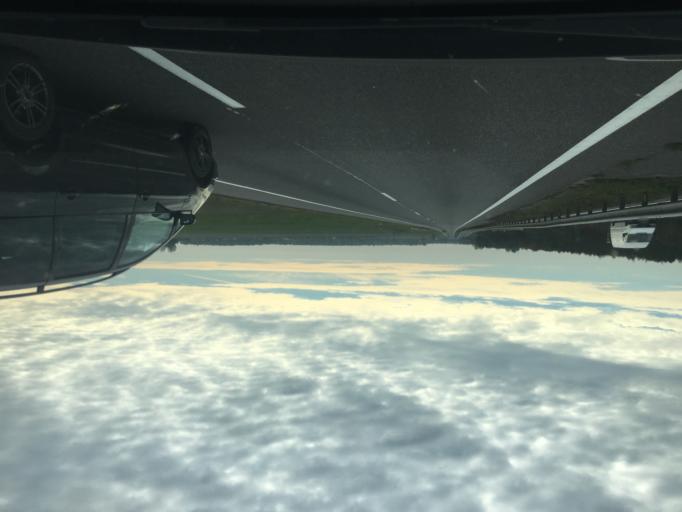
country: BY
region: Minsk
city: Enyerhyetykaw
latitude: 53.6161
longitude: 27.0505
